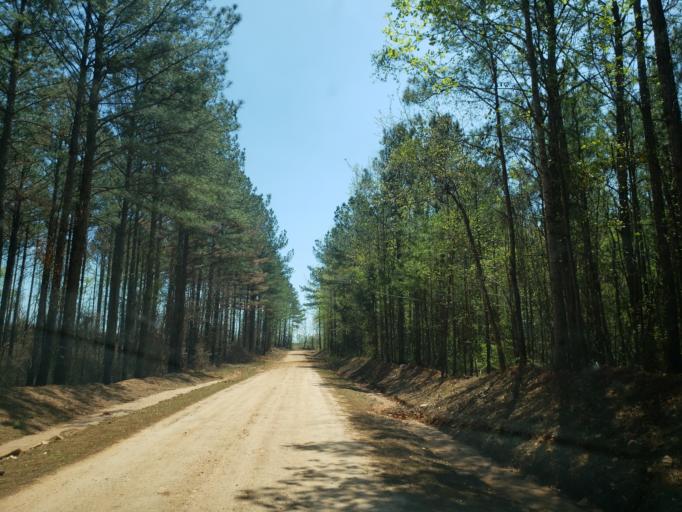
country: US
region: Alabama
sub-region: Tallapoosa County
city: Camp Hill
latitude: 32.6476
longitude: -85.6463
